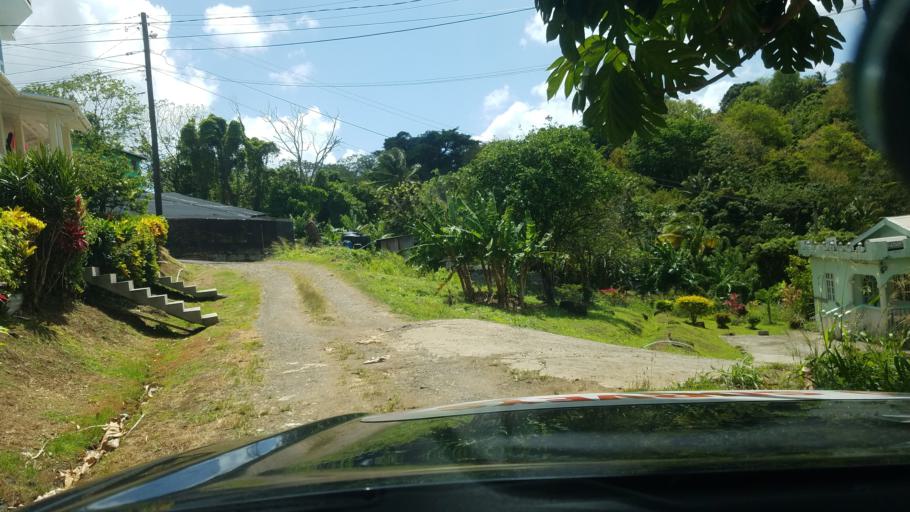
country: LC
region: Castries Quarter
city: Bisee
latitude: 14.0303
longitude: -60.9500
